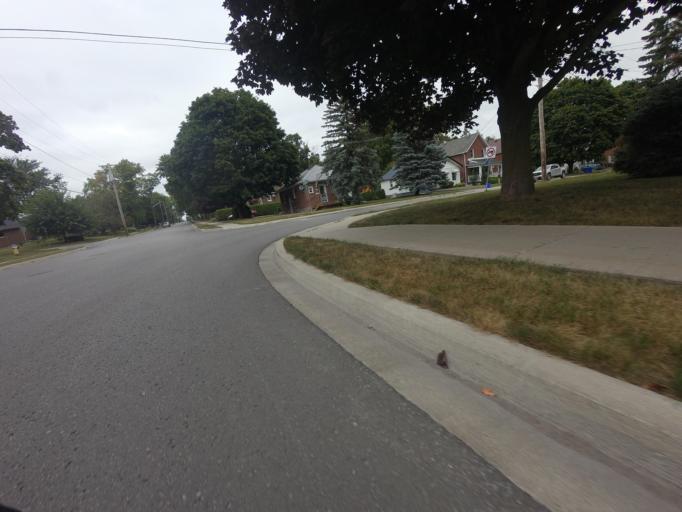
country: CA
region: Ontario
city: Omemee
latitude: 44.3498
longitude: -78.7468
